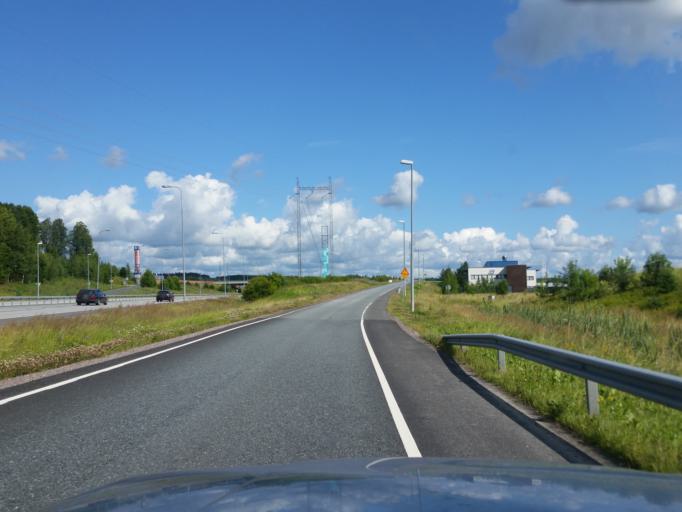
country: FI
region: Uusimaa
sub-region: Helsinki
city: Vihti
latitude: 60.3285
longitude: 24.3349
